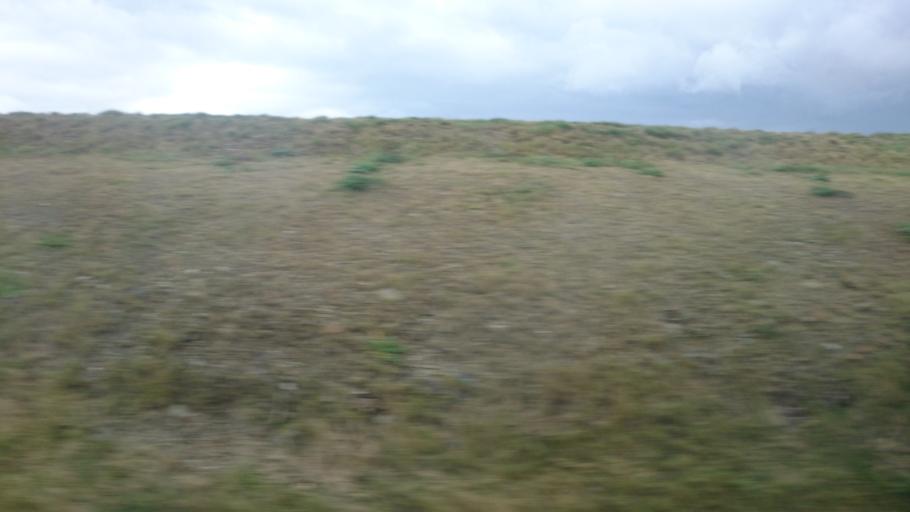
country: DE
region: Thuringia
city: Dittersdorf
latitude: 50.6419
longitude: 11.8117
